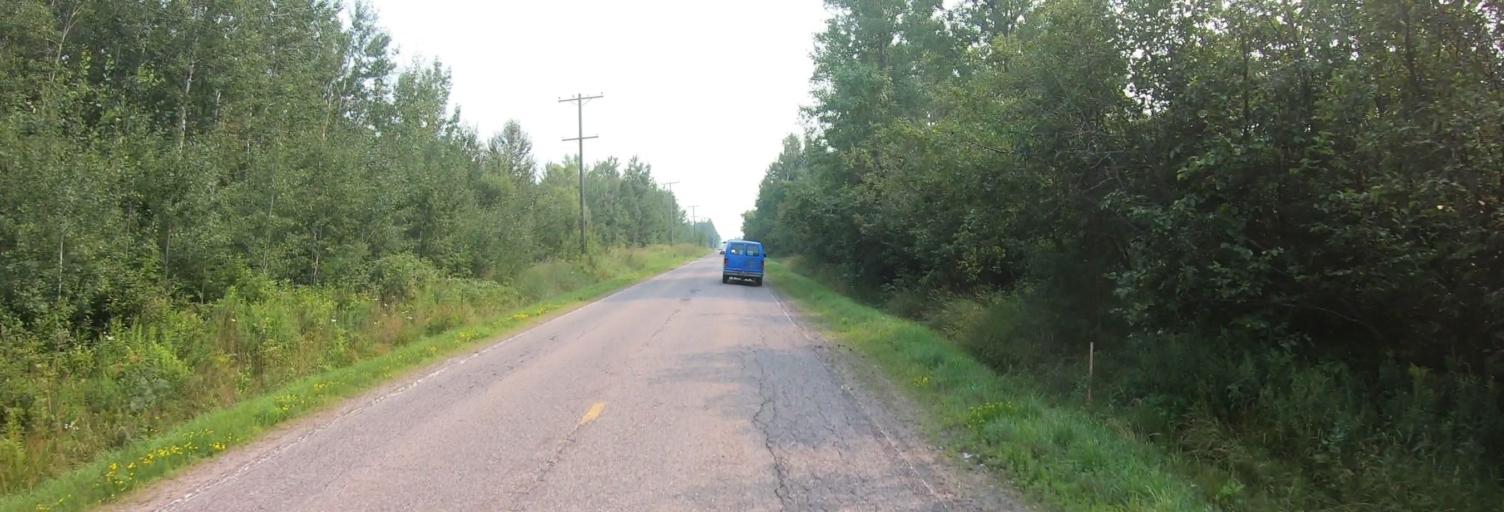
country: US
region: Michigan
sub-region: Chippewa County
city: Sault Ste. Marie
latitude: 46.4661
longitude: -84.3013
